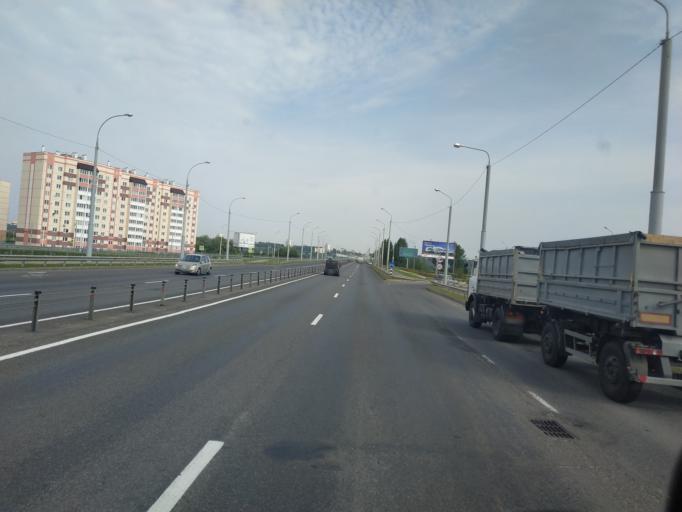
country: BY
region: Mogilev
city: Mahilyow
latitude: 53.8832
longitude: 30.3808
